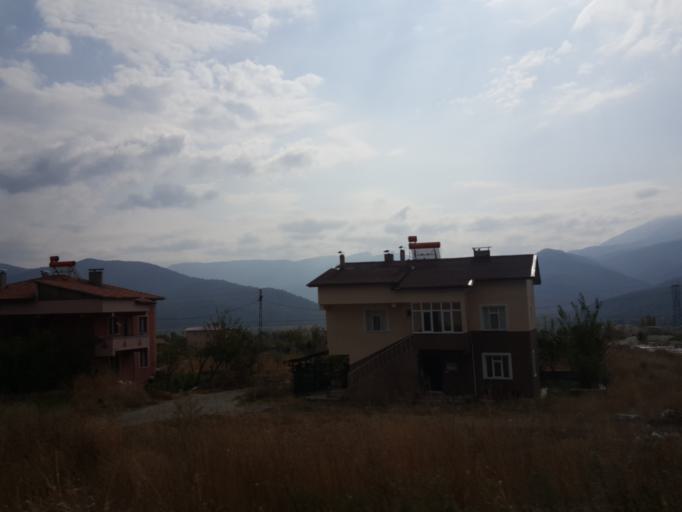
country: TR
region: Corum
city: Hacihamza
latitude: 41.1202
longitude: 34.4102
